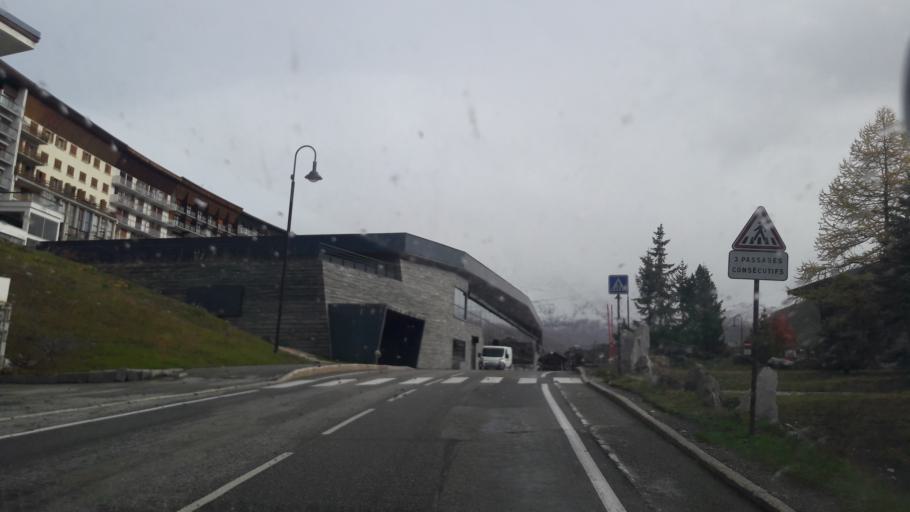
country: FR
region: Rhone-Alpes
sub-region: Departement de la Savoie
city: Tignes
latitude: 45.4674
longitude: 6.9026
